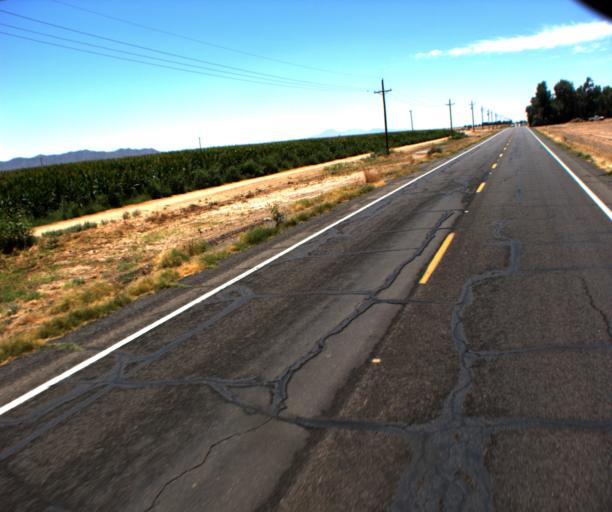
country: US
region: Arizona
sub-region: Pinal County
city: Arizona City
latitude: 32.8797
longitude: -111.6250
